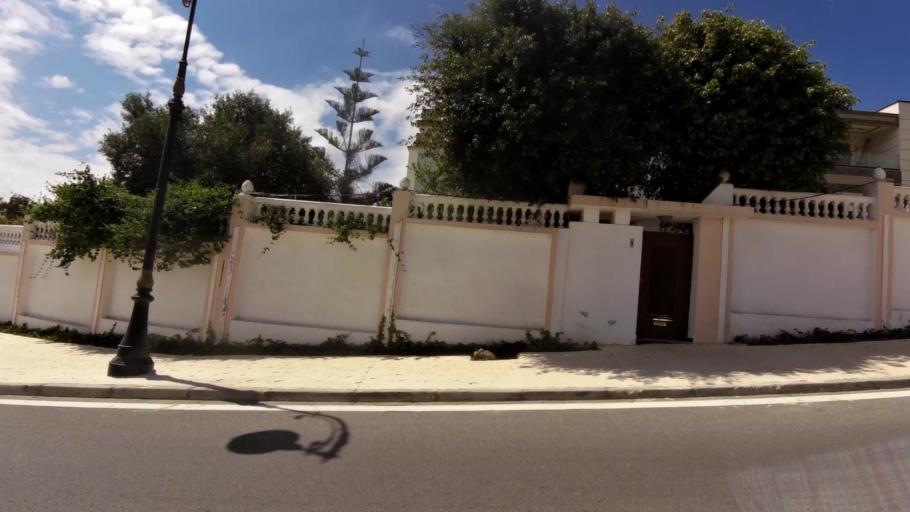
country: MA
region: Tanger-Tetouan
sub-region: Tanger-Assilah
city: Tangier
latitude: 35.7827
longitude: -5.8432
